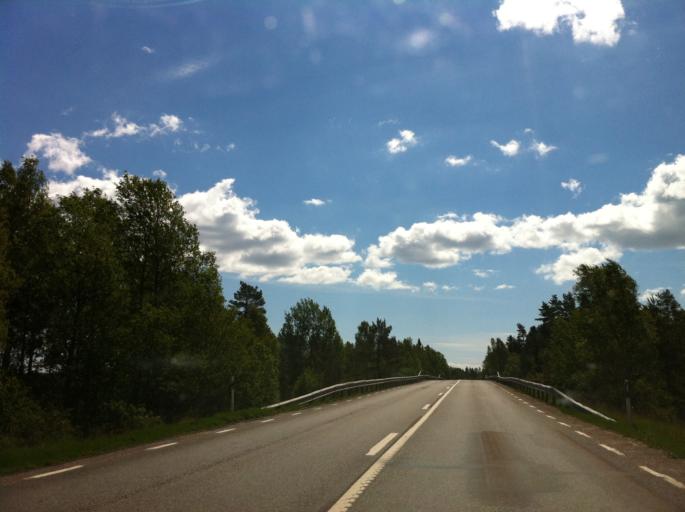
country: SE
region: Vaestra Goetaland
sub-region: Amals Kommun
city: Amal
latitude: 59.0224
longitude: 12.6823
